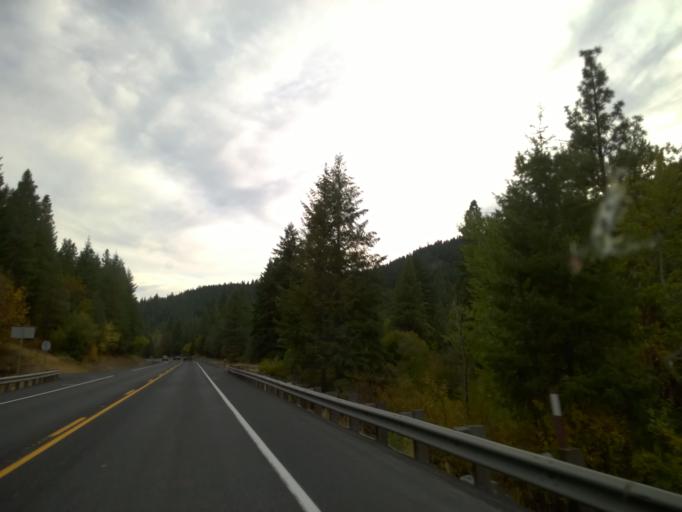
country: US
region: Washington
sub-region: Chelan County
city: Leavenworth
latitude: 47.5087
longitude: -120.6325
